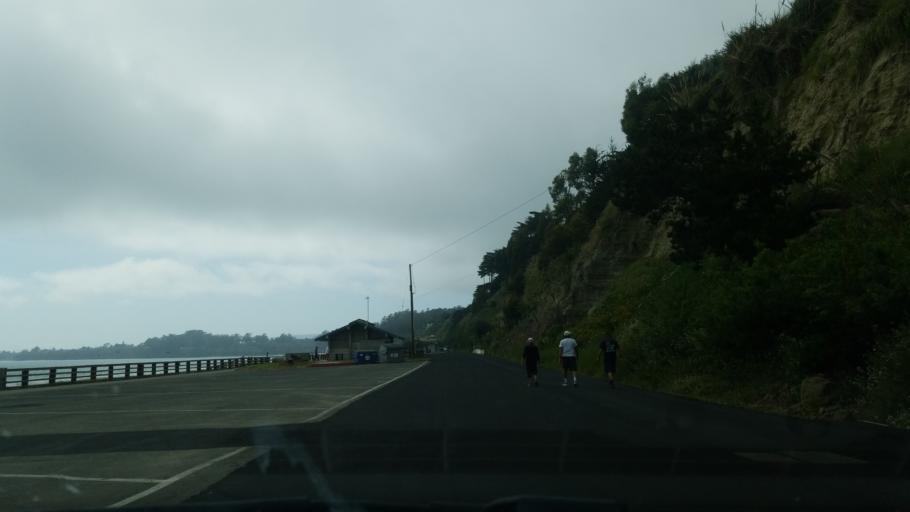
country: US
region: California
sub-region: Santa Cruz County
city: Seacliff
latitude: 36.9738
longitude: -121.9172
